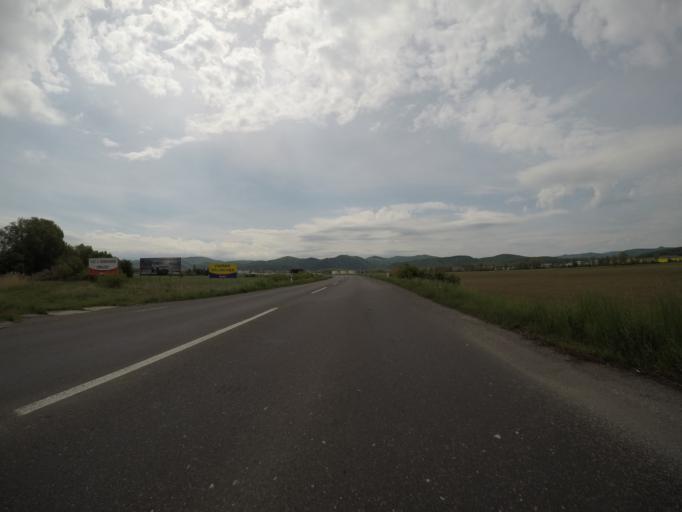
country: SK
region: Banskobystricky
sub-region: Okres Banska Bystrica
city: Zvolen
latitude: 48.5959
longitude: 19.1227
